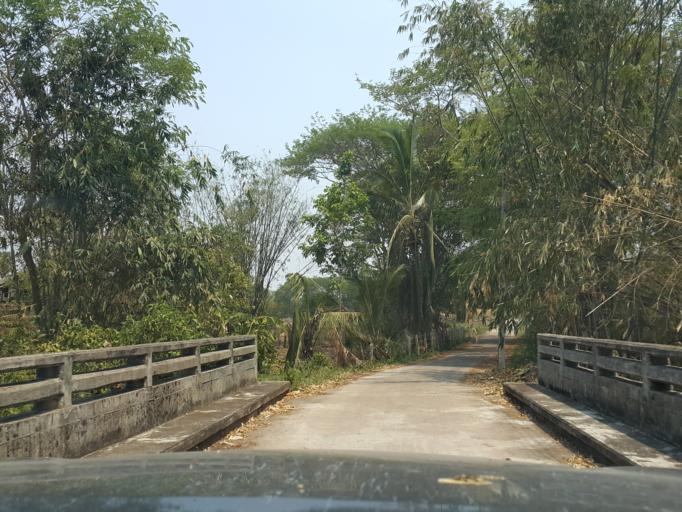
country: TH
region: Lampang
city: Mae Phrik
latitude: 17.5721
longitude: 99.0860
